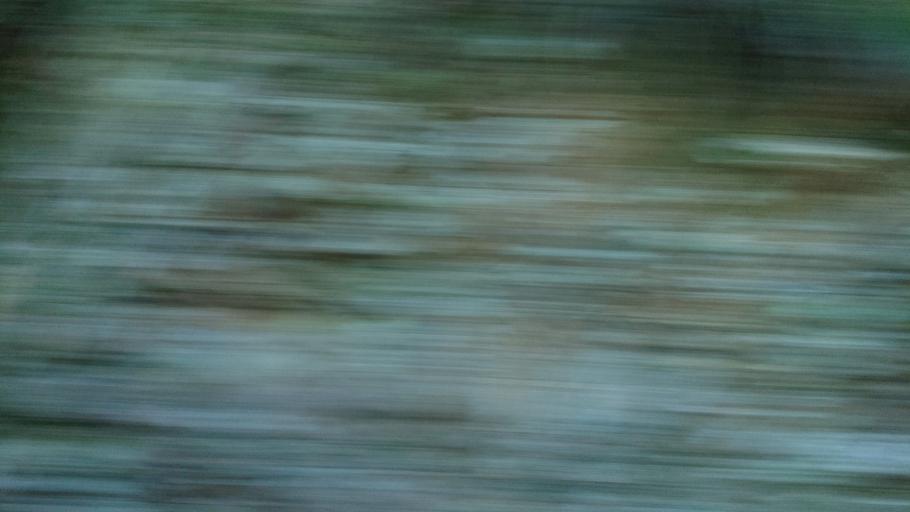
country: TW
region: Taiwan
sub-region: Hualien
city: Hualian
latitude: 24.3746
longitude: 121.3348
